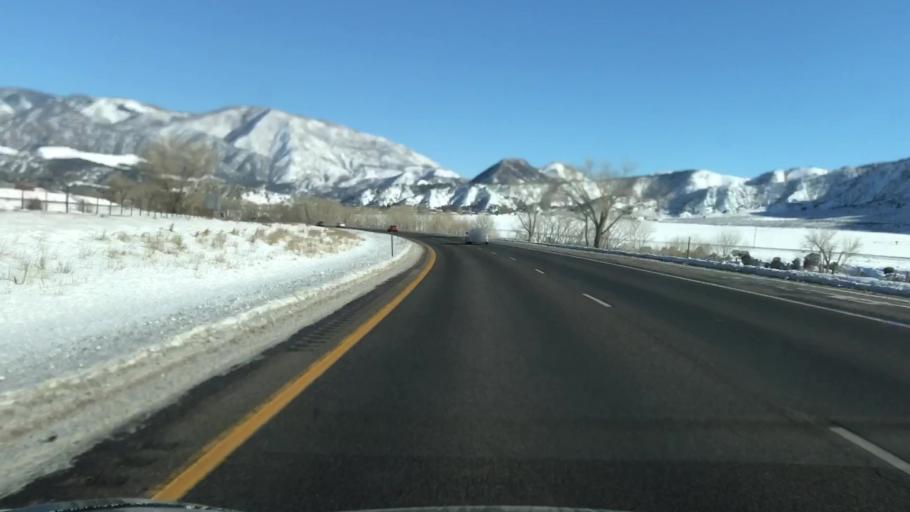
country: US
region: Colorado
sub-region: Garfield County
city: New Castle
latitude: 39.5656
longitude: -107.4932
